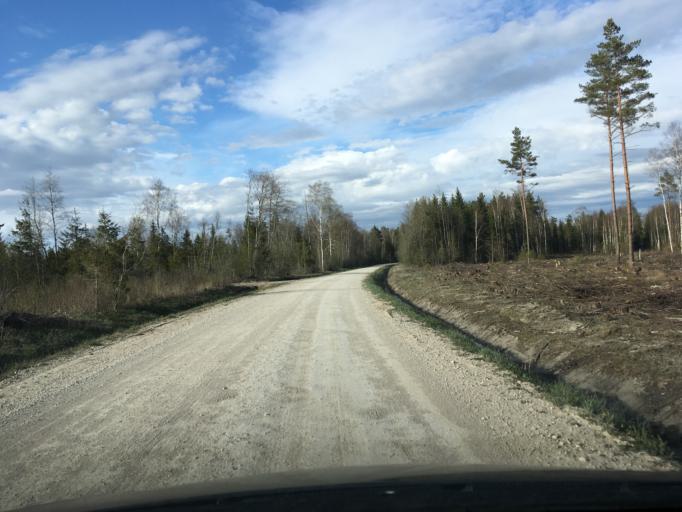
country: EE
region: Raplamaa
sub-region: Maerjamaa vald
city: Marjamaa
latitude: 58.9946
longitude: 24.3679
